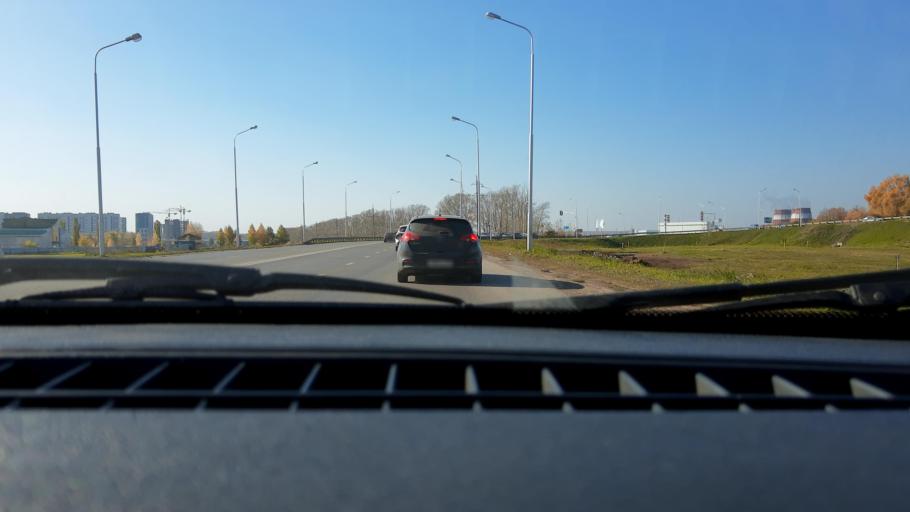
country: RU
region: Bashkortostan
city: Mikhaylovka
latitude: 54.7964
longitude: 55.8637
